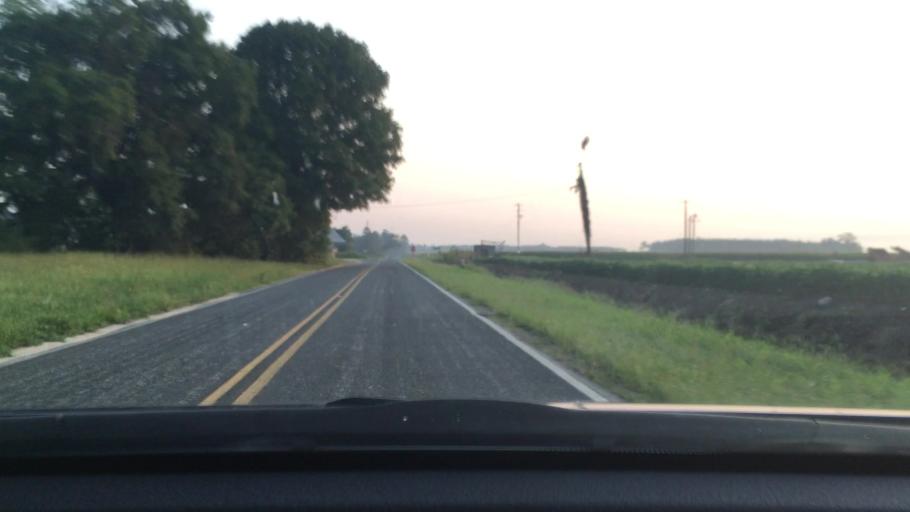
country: US
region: South Carolina
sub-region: Lee County
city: Bishopville
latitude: 34.2153
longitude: -80.1350
